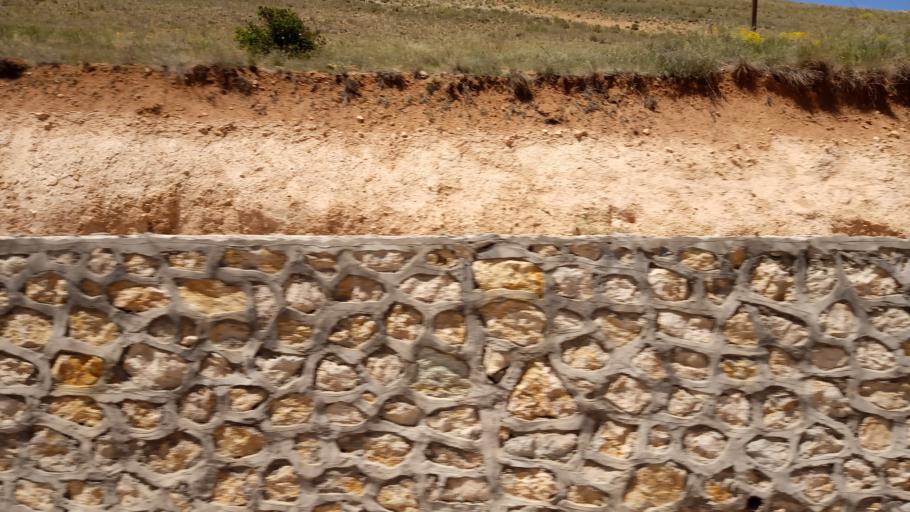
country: TR
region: Malatya
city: Darende
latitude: 38.5931
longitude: 37.4623
